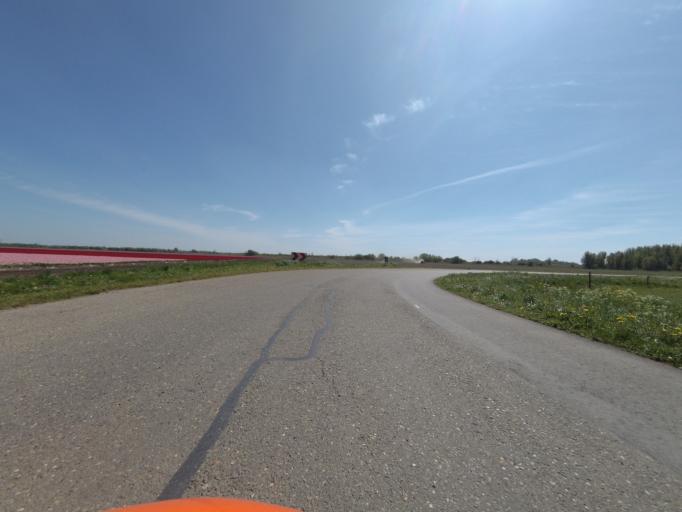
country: NL
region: Flevoland
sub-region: Gemeente Zeewolde
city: Zeewolde
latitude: 52.3751
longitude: 5.5647
